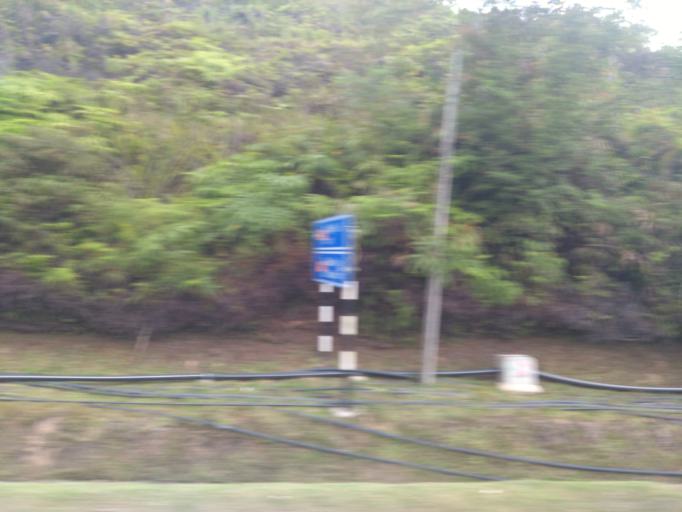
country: MY
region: Pahang
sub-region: Cameron Highlands
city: Tanah Rata
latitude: 4.5827
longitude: 101.4162
